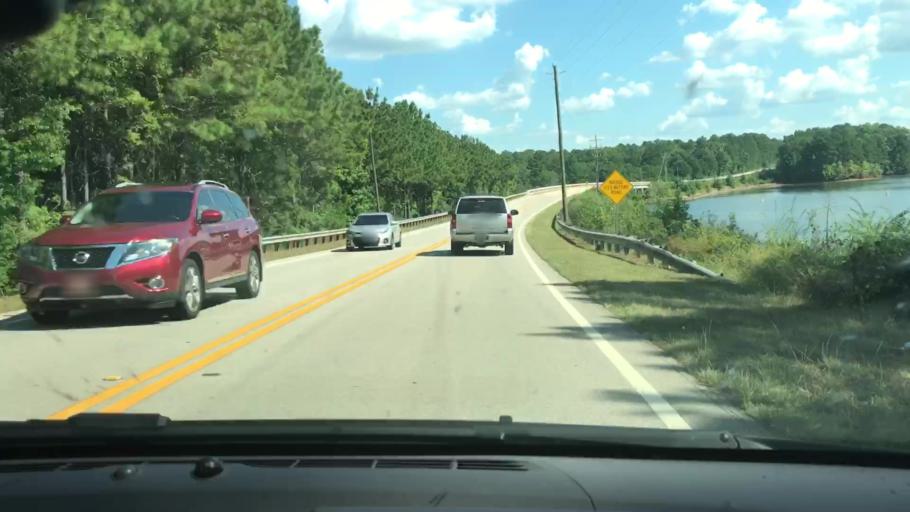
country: US
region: Georgia
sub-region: Troup County
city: La Grange
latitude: 33.0984
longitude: -85.0623
